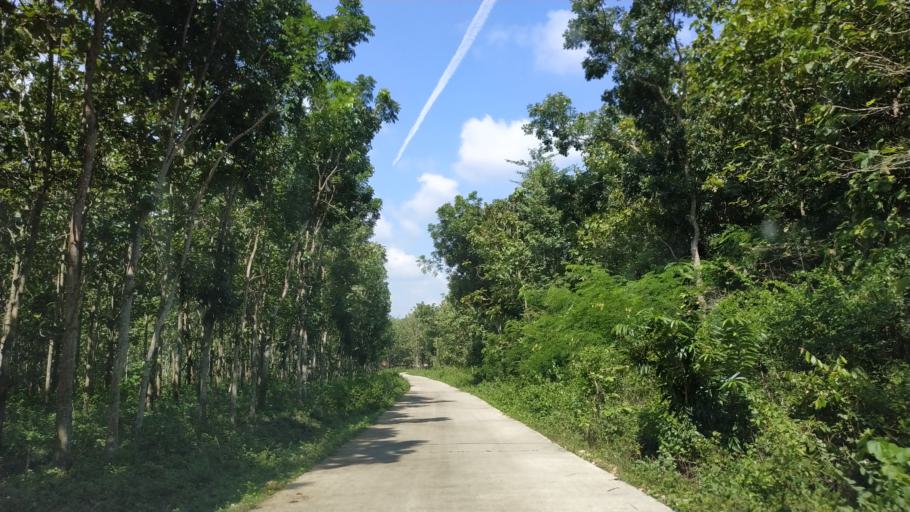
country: ID
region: Central Java
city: Guyangan
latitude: -7.0027
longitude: 111.0889
